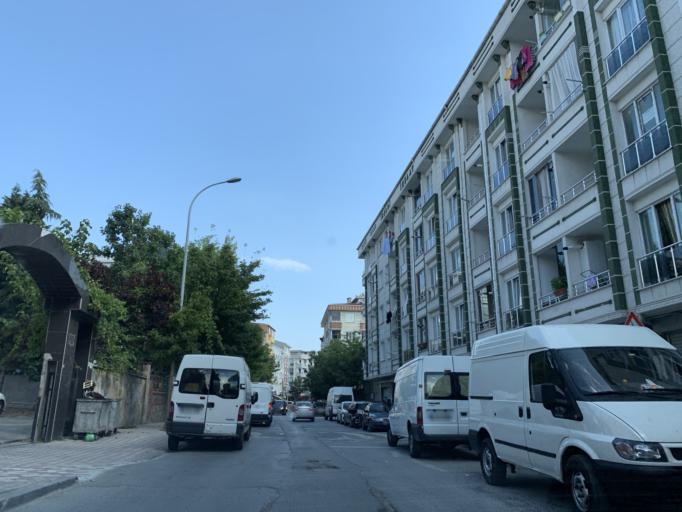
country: TR
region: Istanbul
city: Esenyurt
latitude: 41.0393
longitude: 28.6744
